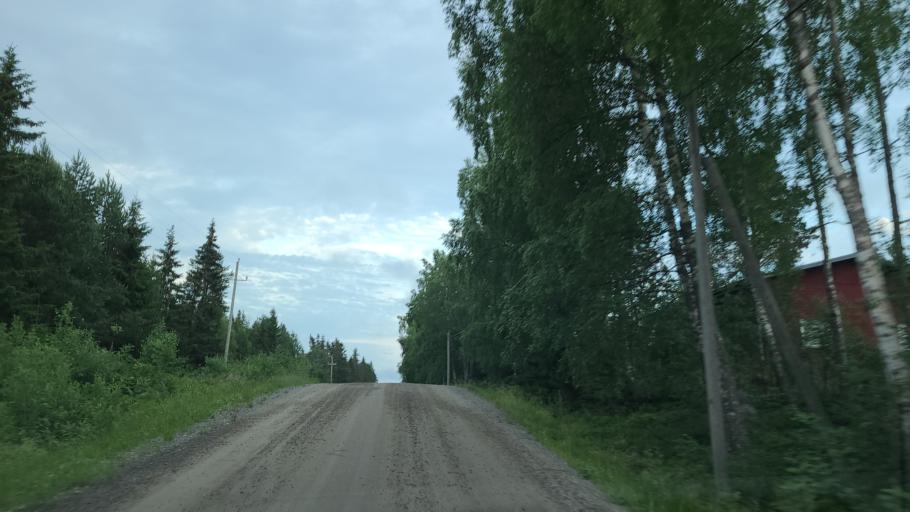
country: FI
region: Ostrobothnia
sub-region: Vaasa
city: Replot
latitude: 63.3215
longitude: 21.1431
